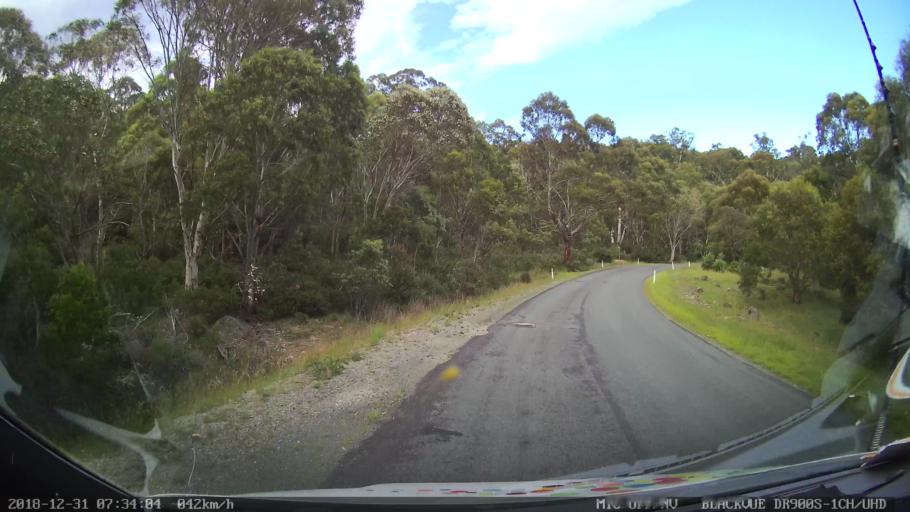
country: AU
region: New South Wales
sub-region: Snowy River
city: Jindabyne
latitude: -36.3353
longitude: 148.4540
